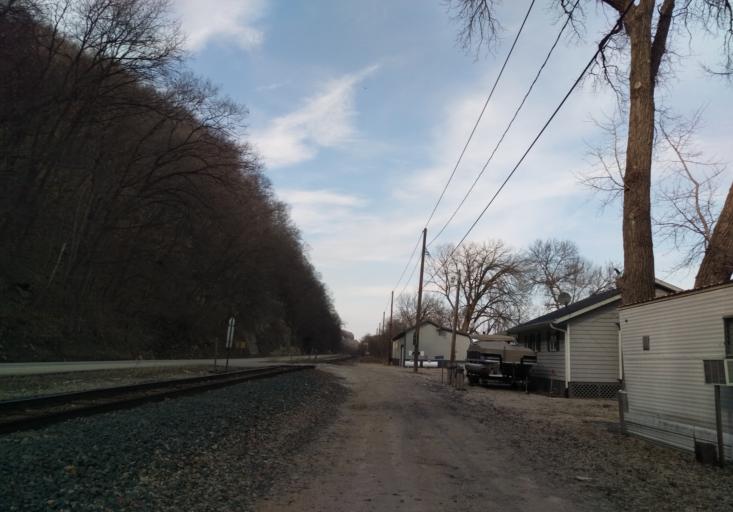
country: US
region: Wisconsin
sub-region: Crawford County
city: Prairie du Chien
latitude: 43.0718
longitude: -91.1801
